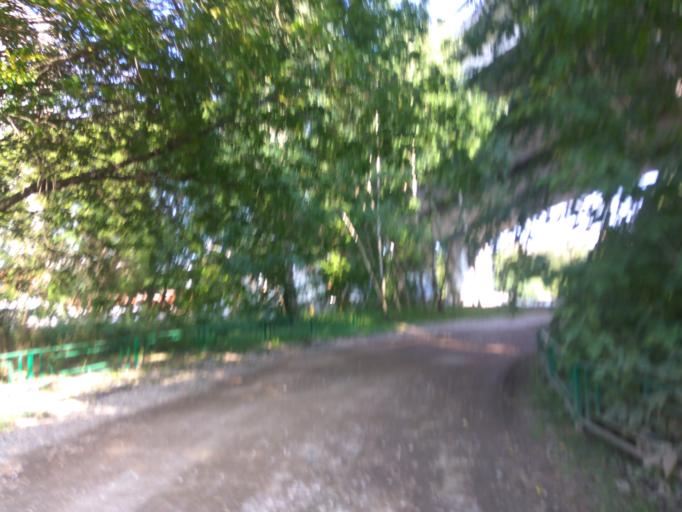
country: RU
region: Moscow
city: Shchukino
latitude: 55.8055
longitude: 37.4444
